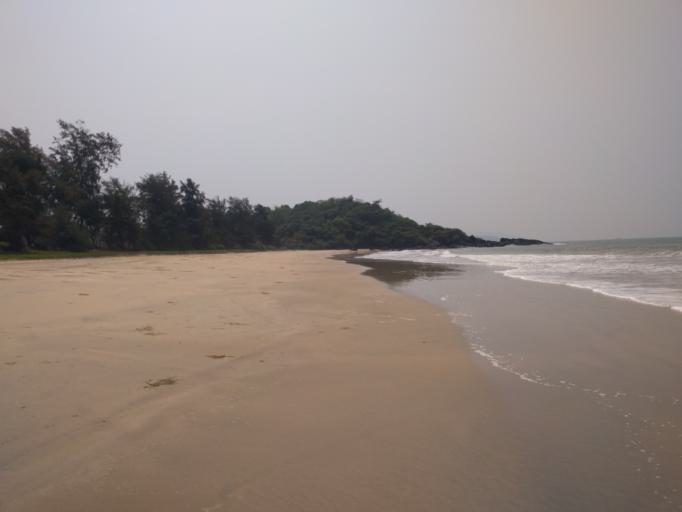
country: IN
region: Karnataka
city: Canacona
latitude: 14.9758
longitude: 74.0428
